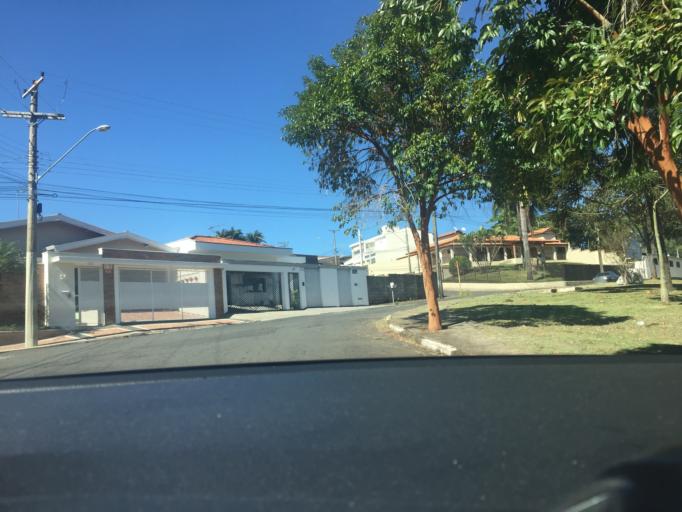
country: BR
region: Sao Paulo
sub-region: Santo Antonio Do Jardim
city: Espirito Santo do Pinhal
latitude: -22.1816
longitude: -46.7437
